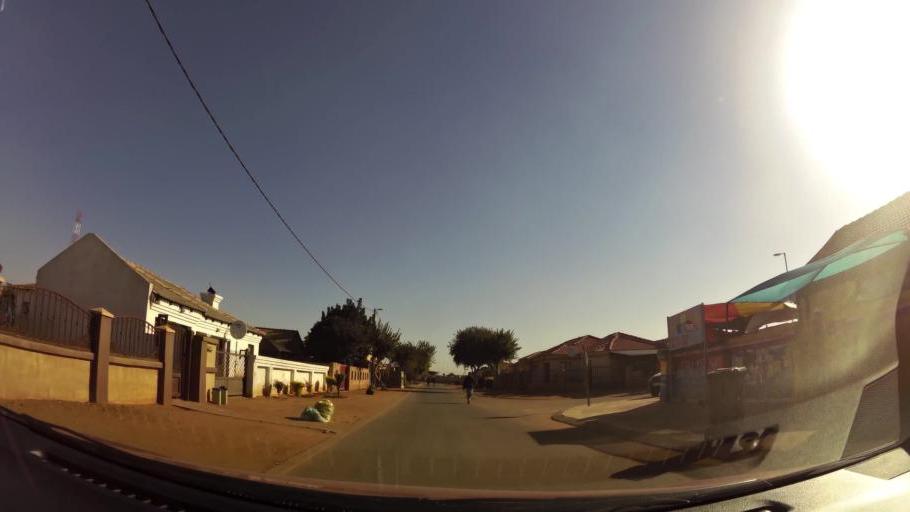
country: ZA
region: Gauteng
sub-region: City of Tshwane Metropolitan Municipality
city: Mabopane
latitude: -25.5743
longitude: 28.1000
